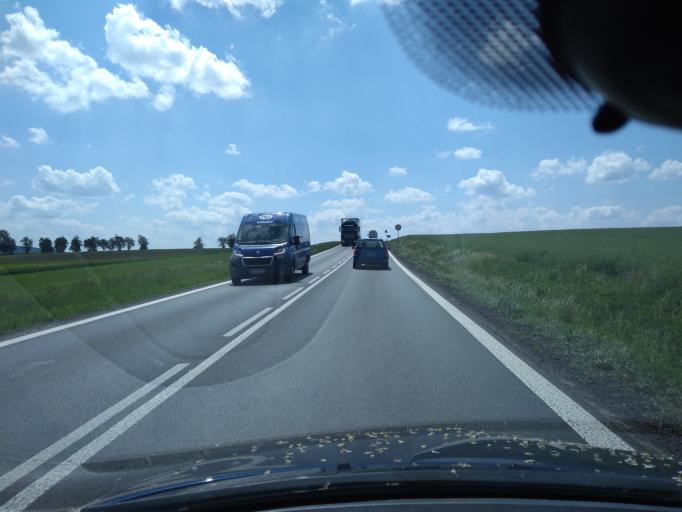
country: CZ
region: Plzensky
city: Prestice
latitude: 49.6032
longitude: 13.3254
